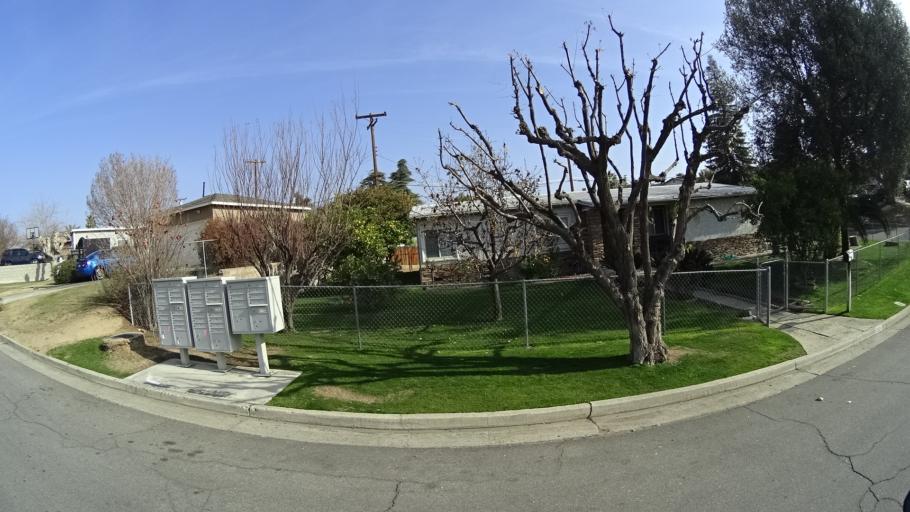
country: US
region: California
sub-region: Kern County
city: Bakersfield
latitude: 35.3879
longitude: -118.9575
